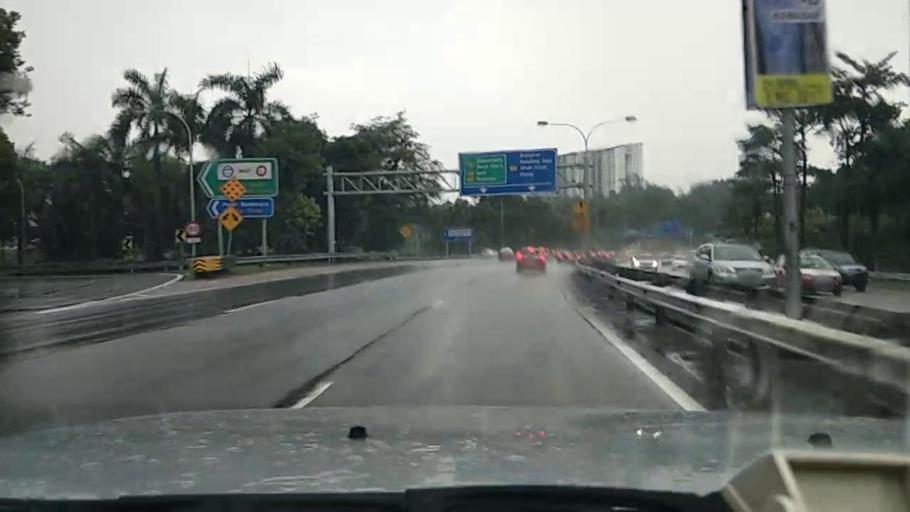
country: MY
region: Kuala Lumpur
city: Kuala Lumpur
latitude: 3.1019
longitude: 101.6963
